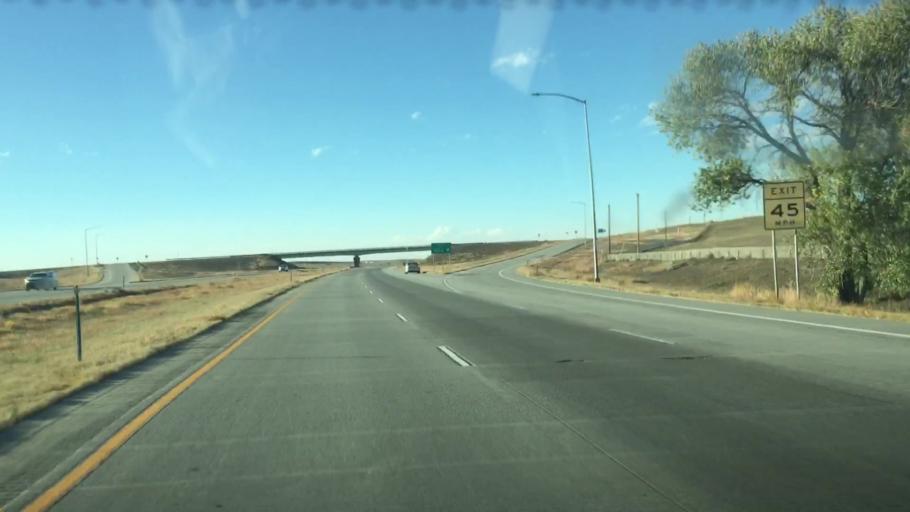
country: US
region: Colorado
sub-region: Lincoln County
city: Limon
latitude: 39.3094
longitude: -103.8227
